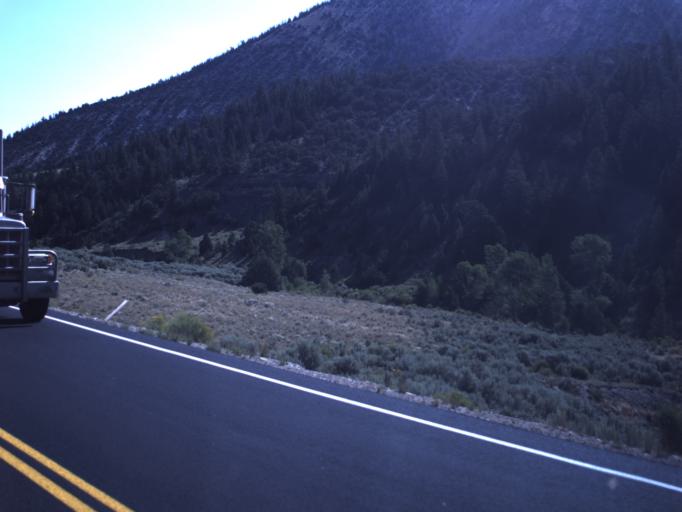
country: US
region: Utah
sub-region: Carbon County
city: Helper
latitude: 39.9453
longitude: -110.6602
